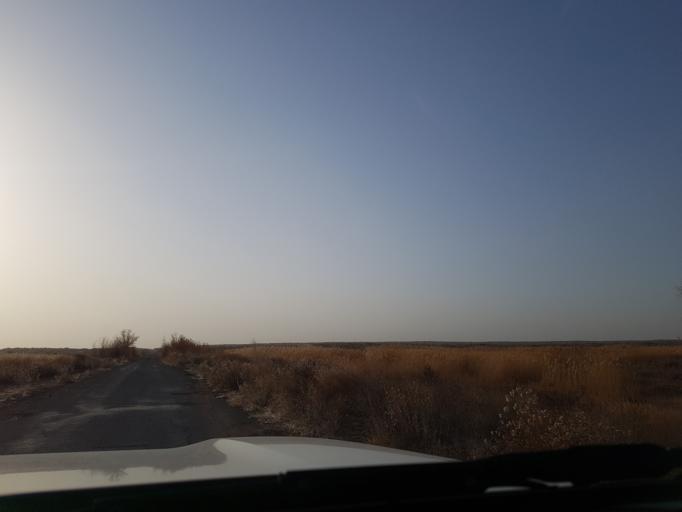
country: UZ
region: Xorazm
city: Hazorasp
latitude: 41.1638
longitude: 60.7523
